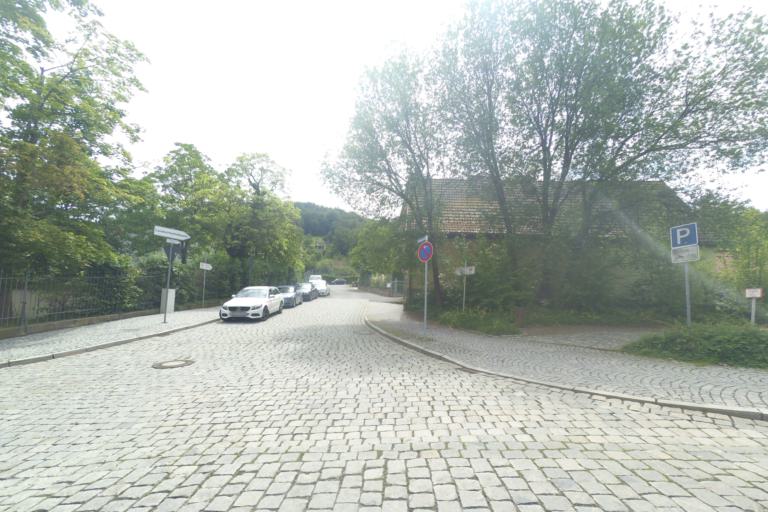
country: DE
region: Bavaria
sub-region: Upper Franconia
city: Kulmbach
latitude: 50.1052
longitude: 11.4600
